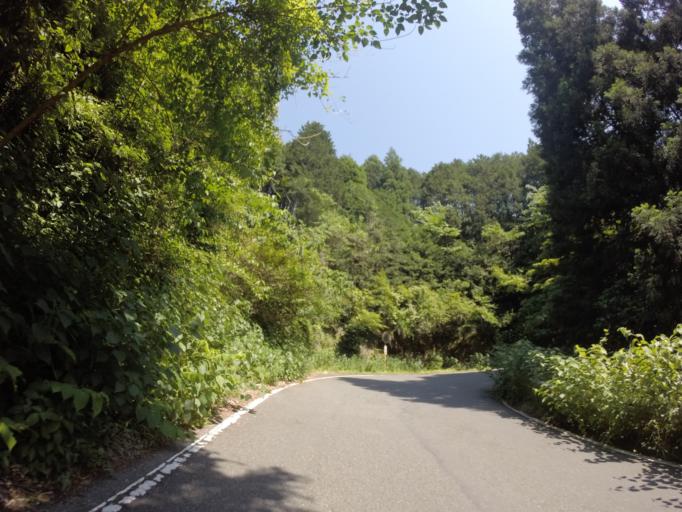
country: JP
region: Shizuoka
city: Fujinomiya
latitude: 35.1551
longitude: 138.5668
